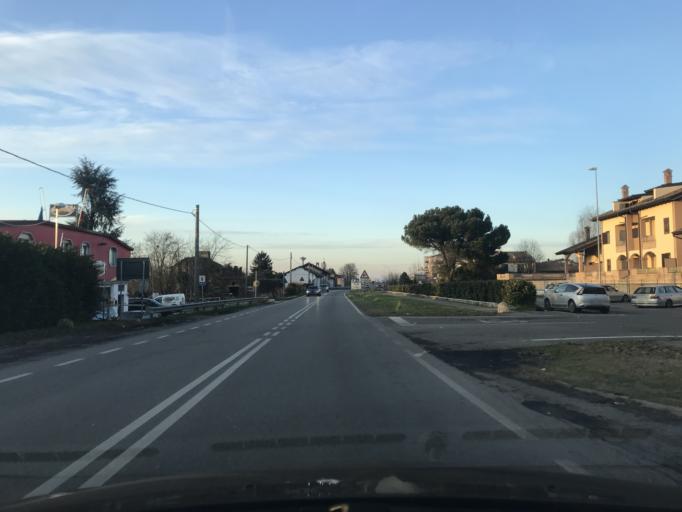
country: IT
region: Lombardy
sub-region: Provincia di Lodi
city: Vidardo
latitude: 45.2551
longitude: 9.3978
